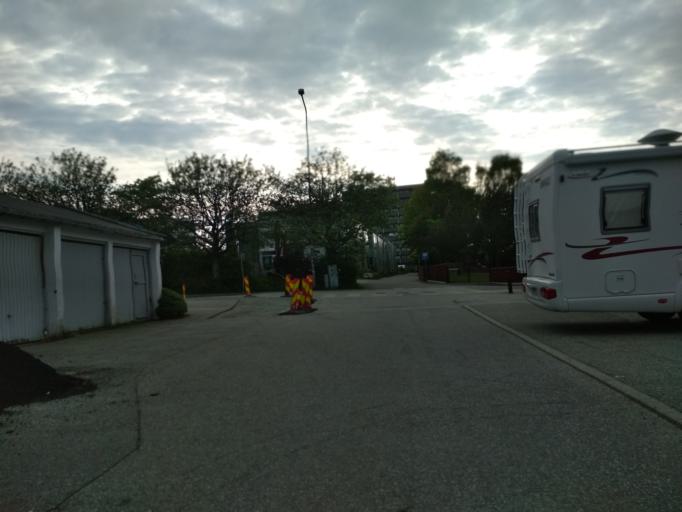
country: NO
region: Rogaland
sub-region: Stavanger
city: Stavanger
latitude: 58.9507
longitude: 5.7296
